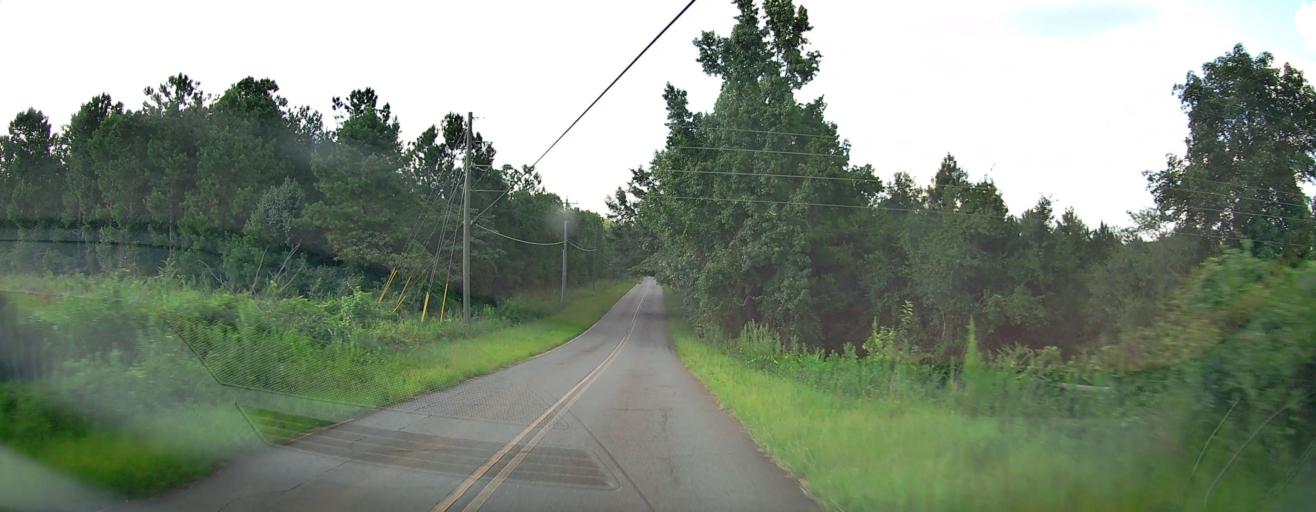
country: US
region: Georgia
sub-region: Houston County
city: Centerville
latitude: 32.5872
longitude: -83.6524
